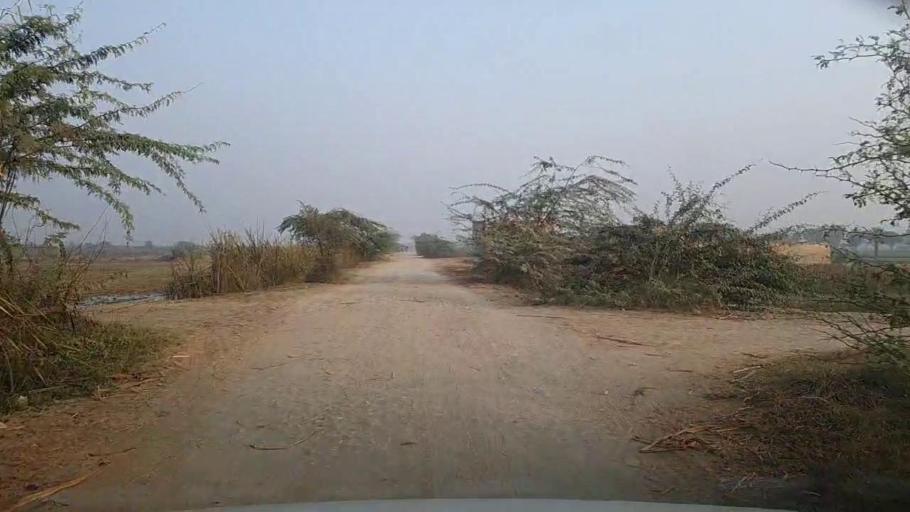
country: PK
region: Sindh
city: Bozdar
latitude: 27.0752
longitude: 68.5857
